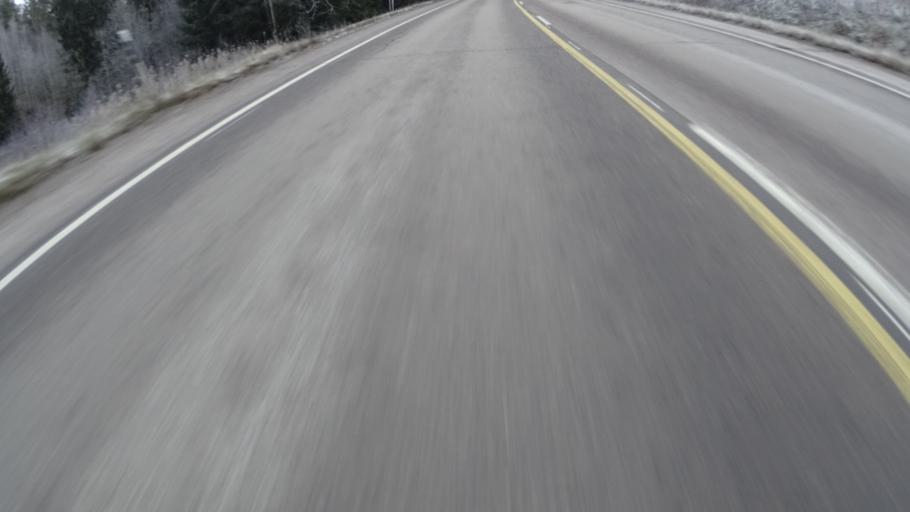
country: FI
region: Uusimaa
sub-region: Helsinki
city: Nurmijaervi
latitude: 60.4176
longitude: 24.7329
